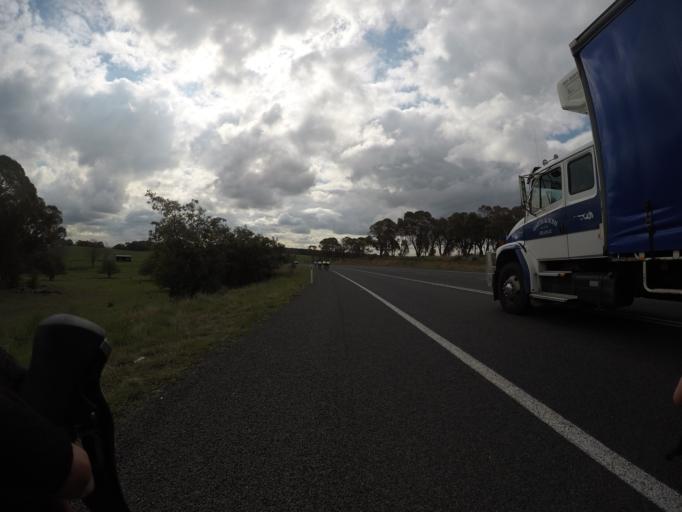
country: AU
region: New South Wales
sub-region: Blayney
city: Blayney
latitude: -33.4269
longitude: 149.3137
